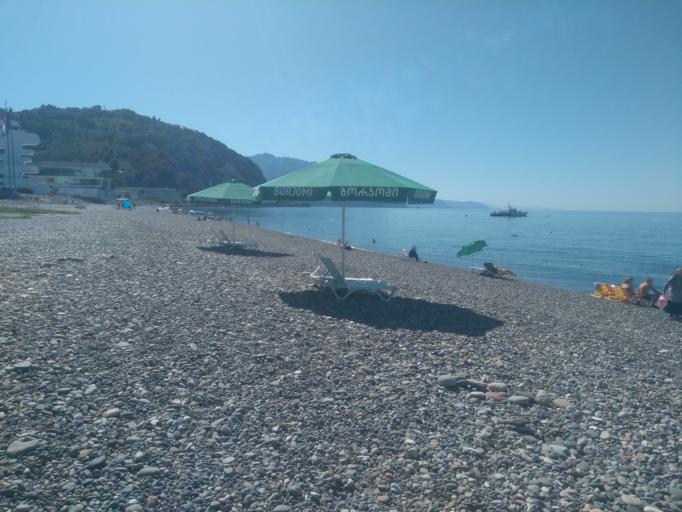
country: TR
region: Artvin
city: Kemalpasa
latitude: 41.5241
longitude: 41.5483
